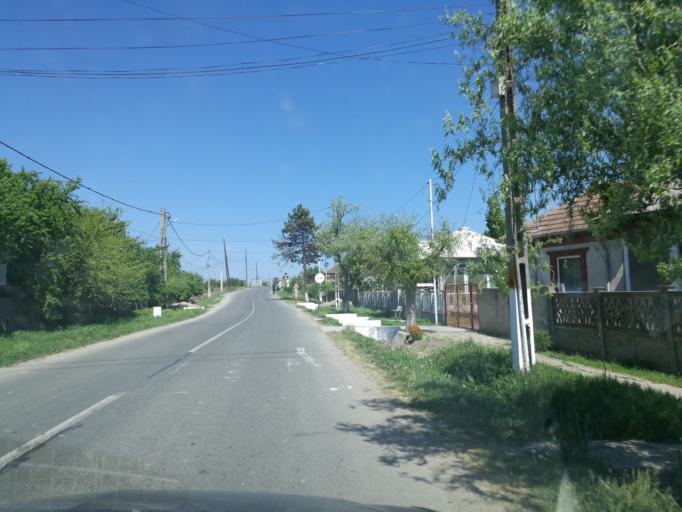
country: RO
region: Ialomita
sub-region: Comuna Adancata
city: Adancata
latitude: 44.7723
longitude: 26.4326
